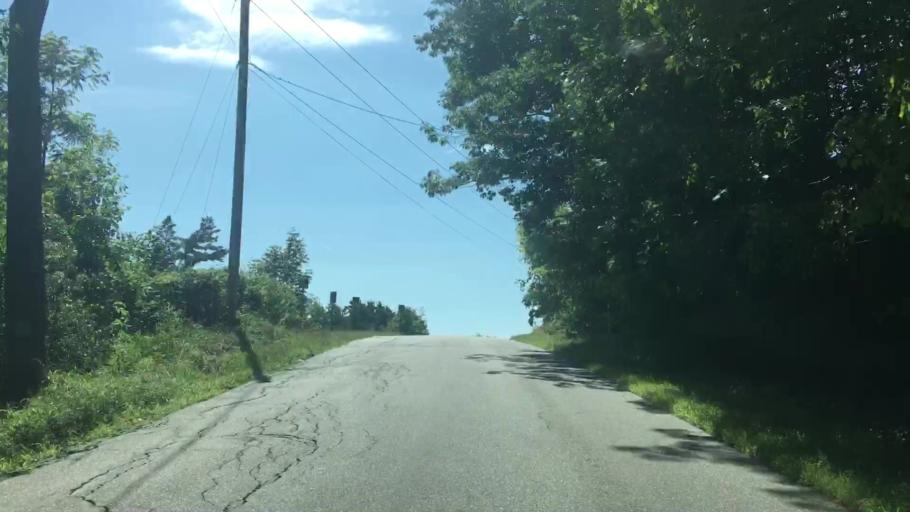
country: US
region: Maine
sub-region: Kennebec County
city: Monmouth
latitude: 44.2056
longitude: -69.9539
